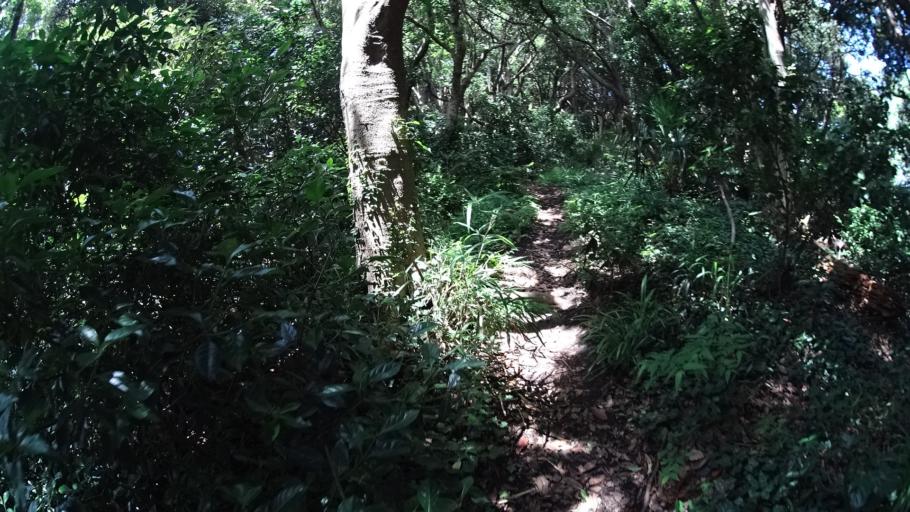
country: JP
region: Kanagawa
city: Yokosuka
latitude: 35.2151
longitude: 139.6699
